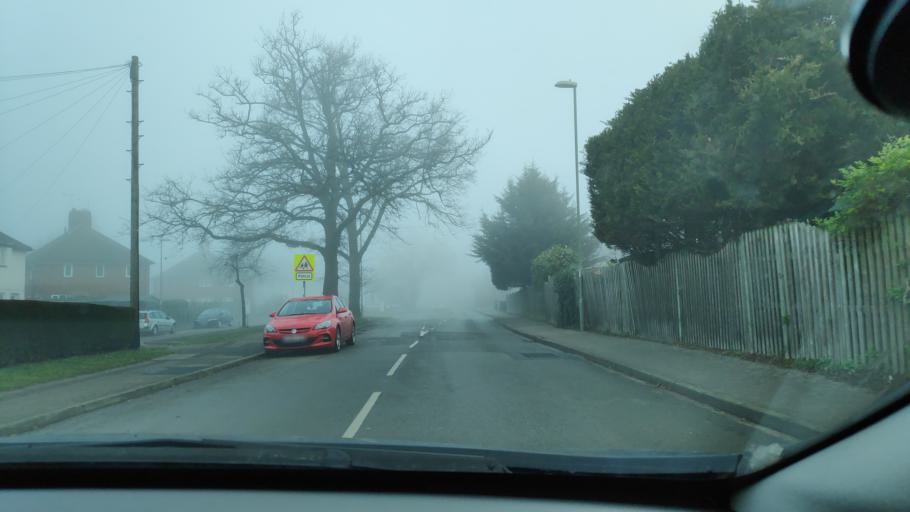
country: GB
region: England
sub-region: Hampshire
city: Farnborough
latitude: 51.2823
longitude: -0.7381
